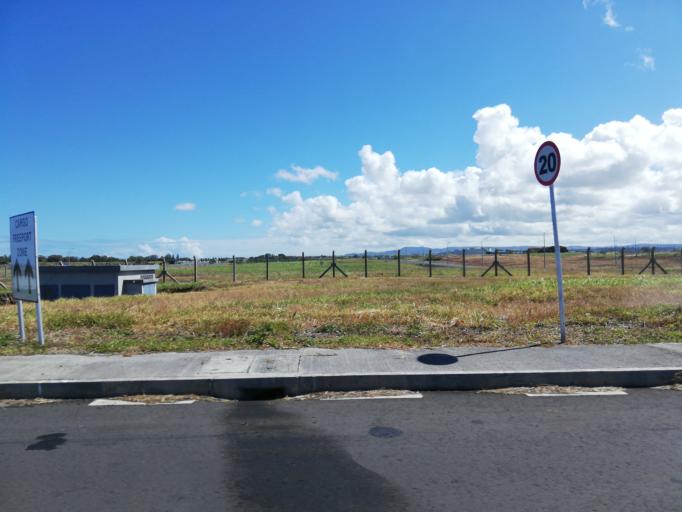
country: MU
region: Grand Port
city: Beau Vallon
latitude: -20.4417
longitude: 57.6899
